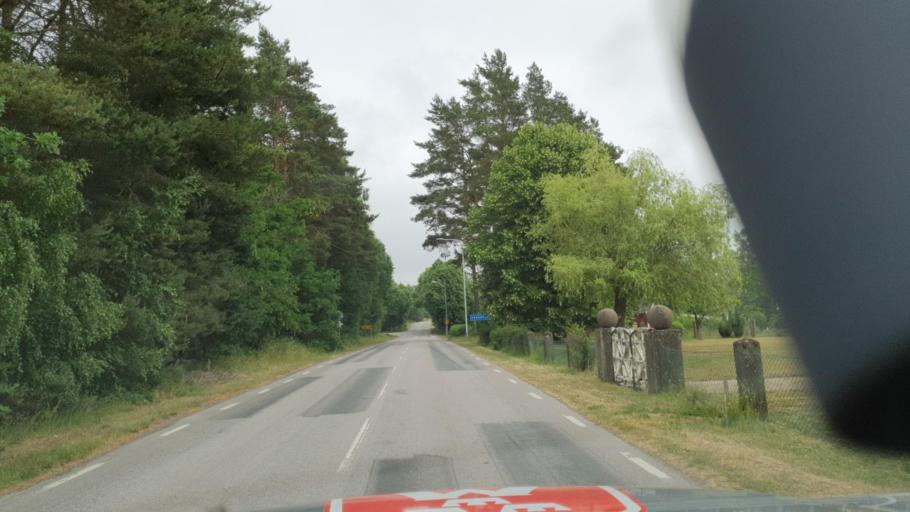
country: SE
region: Kalmar
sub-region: Kalmar Kommun
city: Ljungbyholm
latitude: 56.5921
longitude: 16.1491
